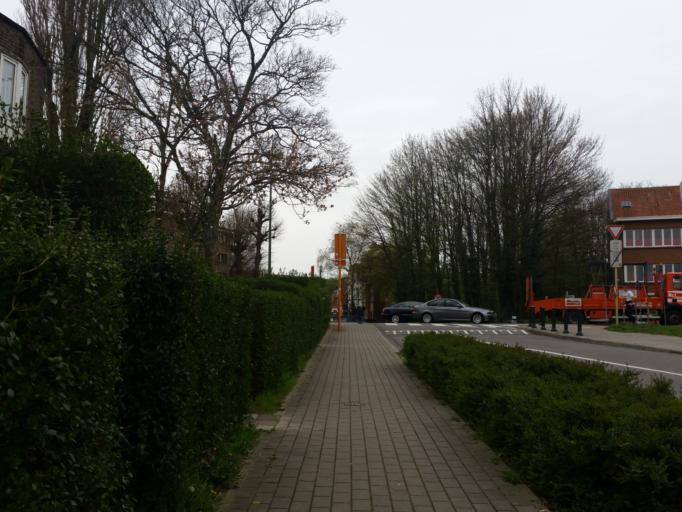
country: BE
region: Flanders
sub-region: Provincie Vlaams-Brabant
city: Kraainem
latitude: 50.8477
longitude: 4.4574
